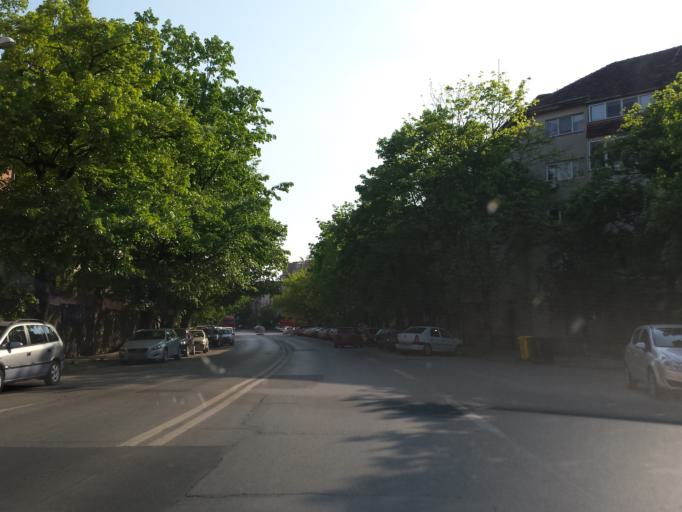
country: RO
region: Timis
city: Timisoara
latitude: 45.7550
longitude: 21.2529
